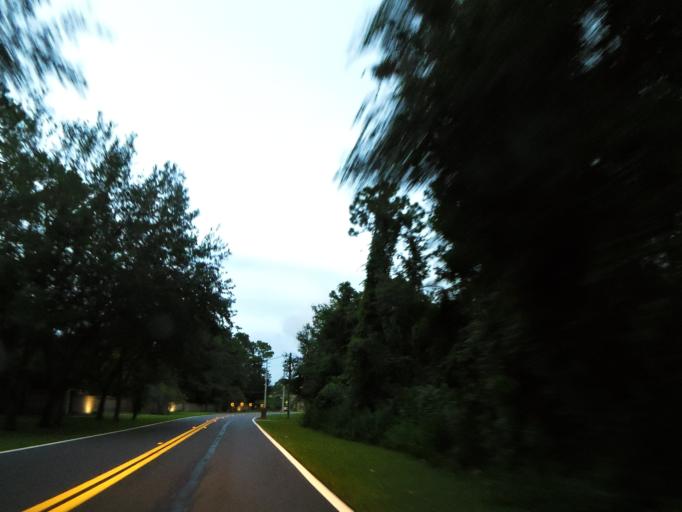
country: US
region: Florida
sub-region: Duval County
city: Jacksonville
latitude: 30.3811
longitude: -81.6096
